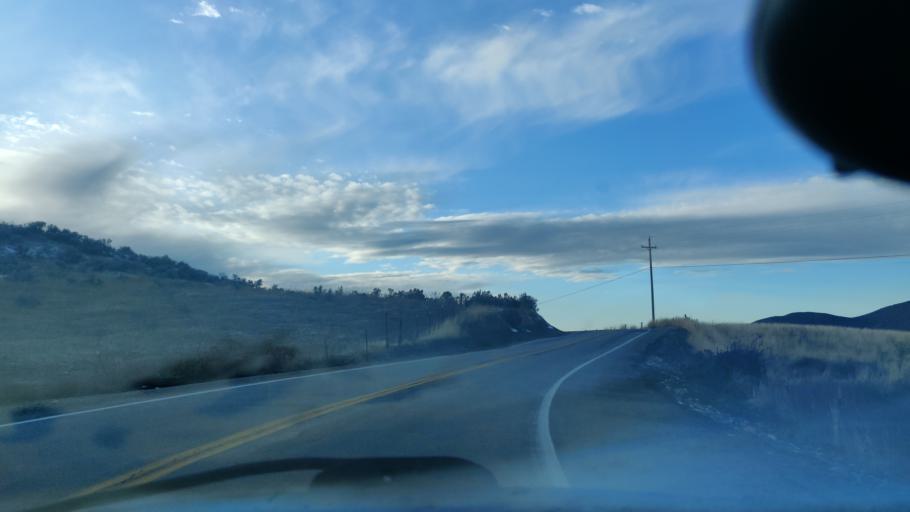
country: US
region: Idaho
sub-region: Ada County
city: Eagle
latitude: 43.7291
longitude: -116.2796
